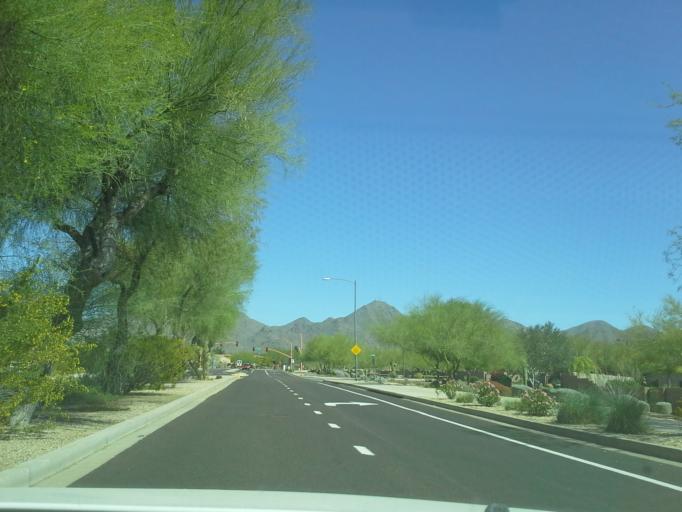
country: US
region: Arizona
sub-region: Maricopa County
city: Scottsdale
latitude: 33.6125
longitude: -111.8700
